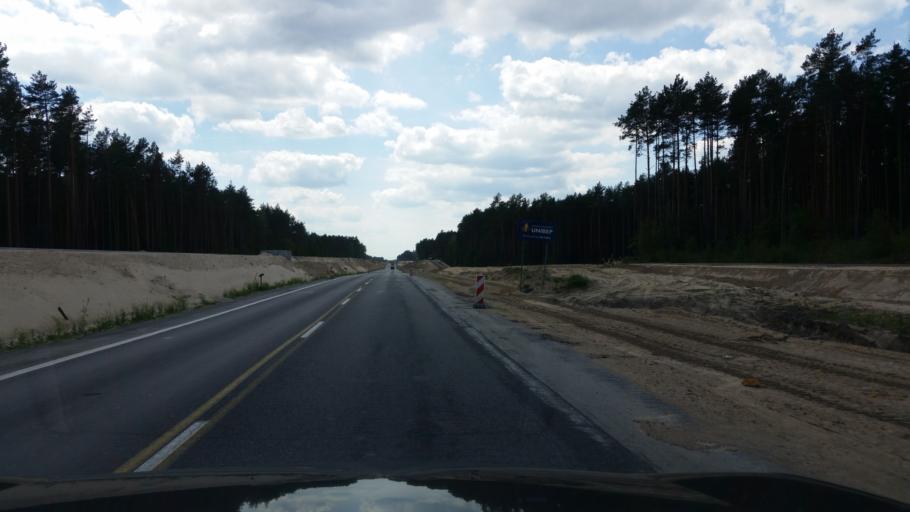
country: PL
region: Masovian Voivodeship
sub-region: Powiat ostrowski
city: Brok
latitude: 52.7446
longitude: 21.7664
